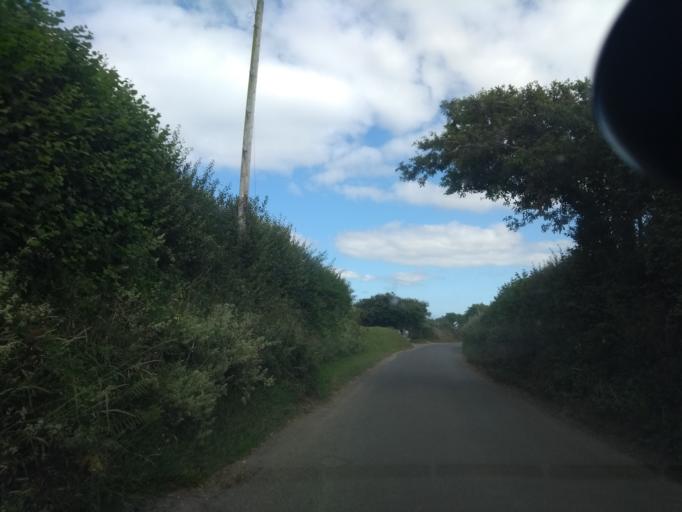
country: GB
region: England
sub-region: Devon
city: Modbury
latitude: 50.3093
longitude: -3.8761
